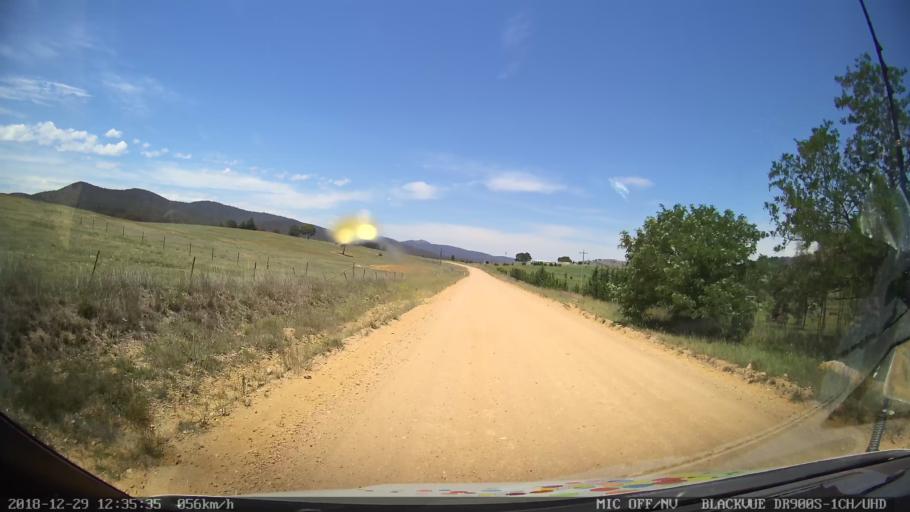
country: AU
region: Australian Capital Territory
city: Macarthur
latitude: -35.5634
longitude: 149.2234
